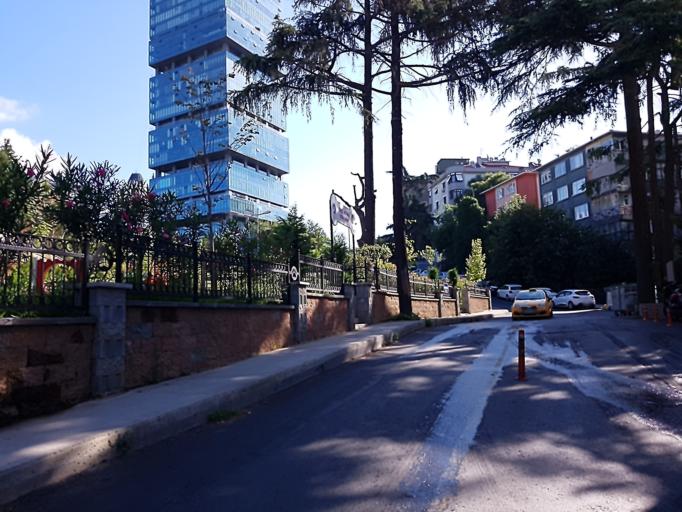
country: TR
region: Istanbul
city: Sisli
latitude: 41.0719
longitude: 29.0103
